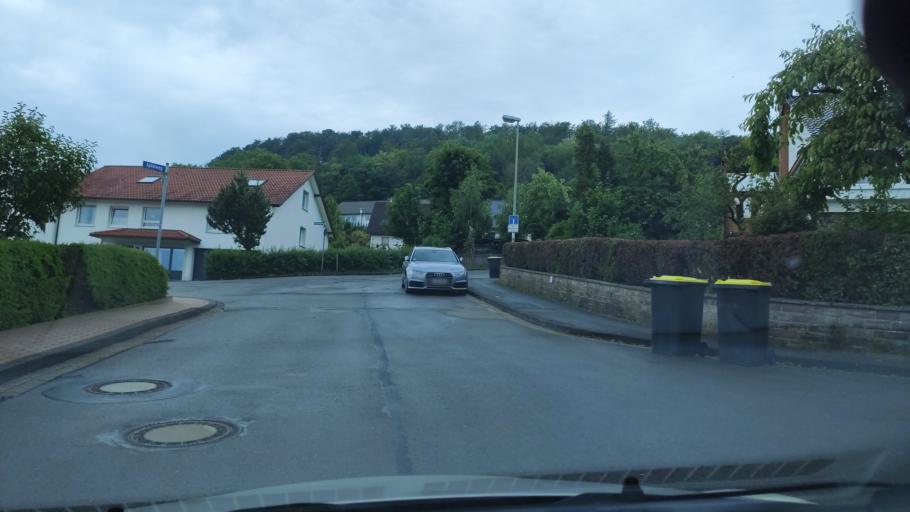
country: DE
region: North Rhine-Westphalia
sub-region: Regierungsbezirk Detmold
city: Hoexter
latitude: 51.7657
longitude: 9.3717
